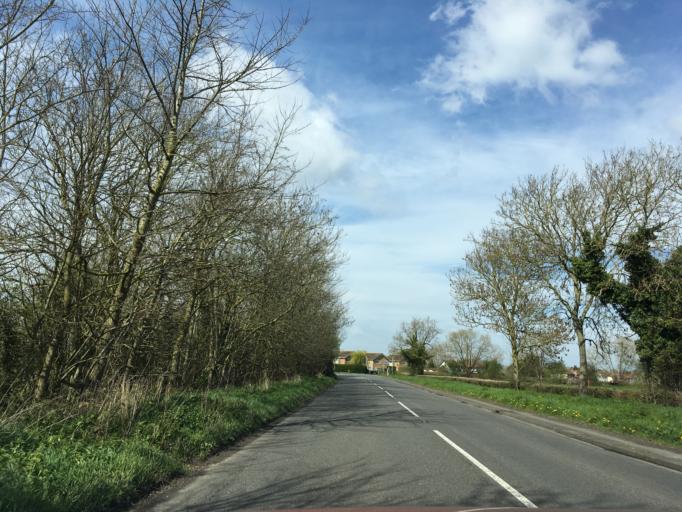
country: GB
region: England
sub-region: South Gloucestershire
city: Severn Beach
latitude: 51.5464
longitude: -2.6273
